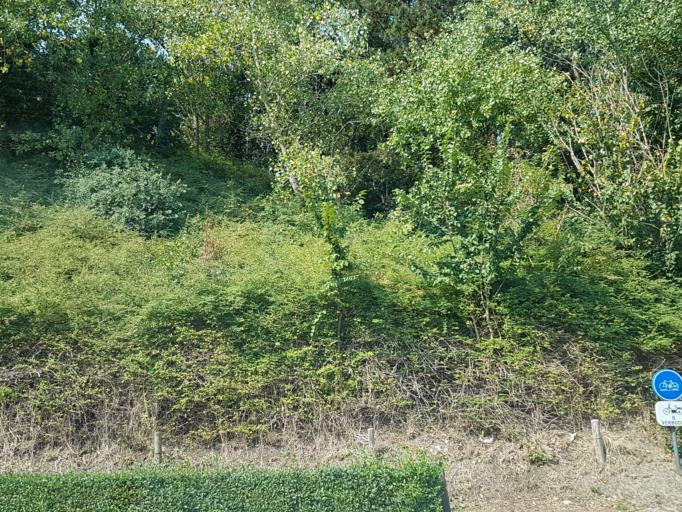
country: BE
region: Flanders
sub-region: Provincie West-Vlaanderen
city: De Haan
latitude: 51.2702
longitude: 3.0270
